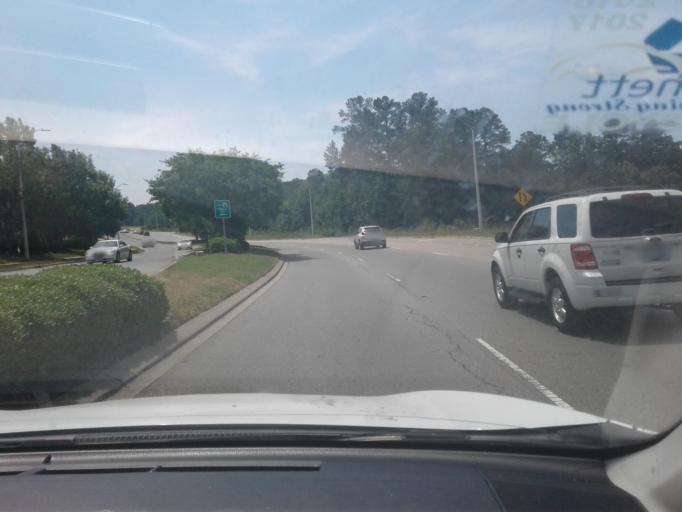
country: US
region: North Carolina
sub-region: Wake County
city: Garner
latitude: 35.6953
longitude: -78.5846
